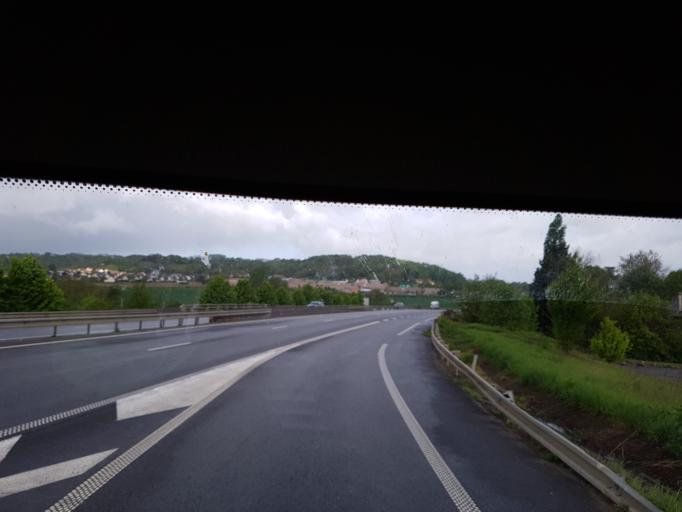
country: FR
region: Picardie
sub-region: Departement de l'Aisne
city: Courmelles
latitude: 49.3606
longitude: 3.3172
